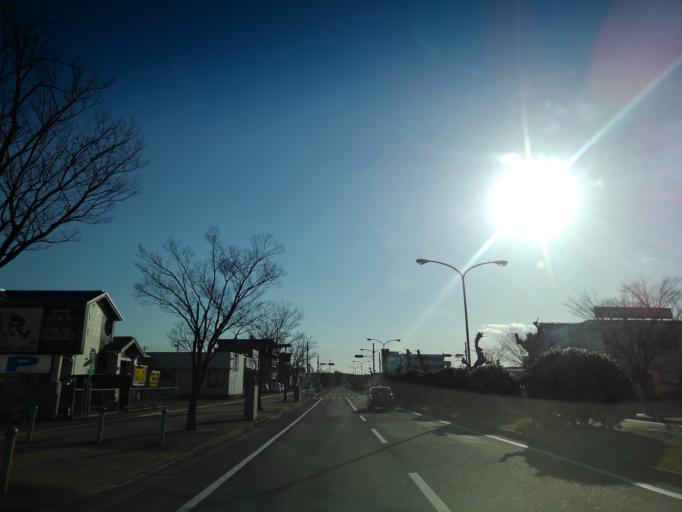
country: JP
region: Chiba
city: Kimitsu
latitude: 35.3329
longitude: 139.8942
